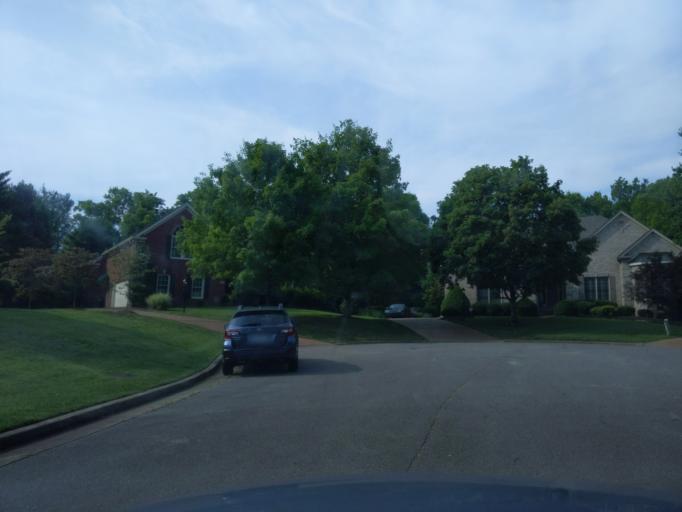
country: US
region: Tennessee
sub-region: Williamson County
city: Brentwood Estates
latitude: 36.0247
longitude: -86.7450
